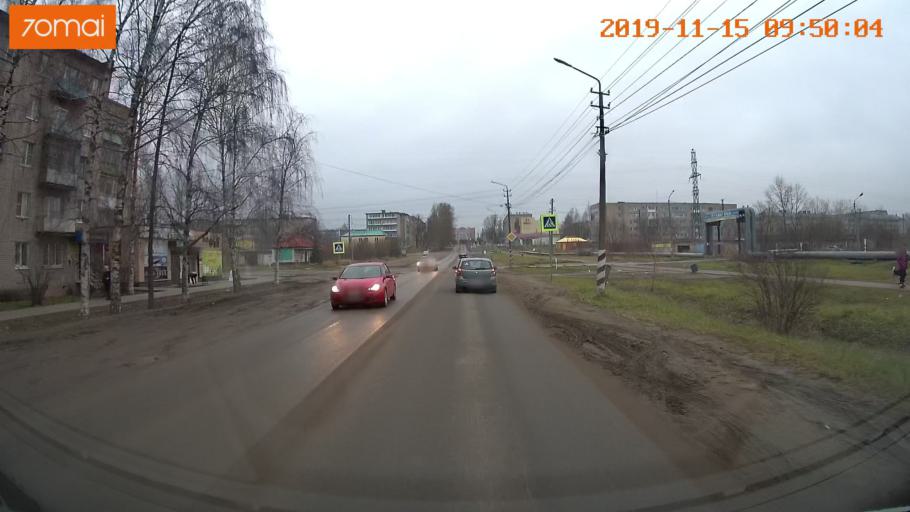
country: RU
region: Vologda
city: Sheksna
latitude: 59.2309
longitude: 38.5134
